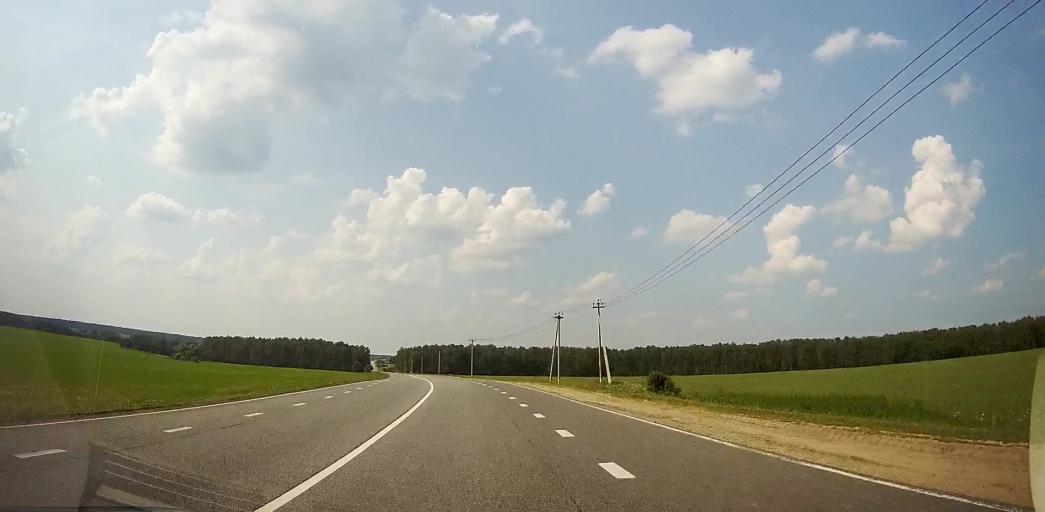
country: RU
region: Moskovskaya
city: Malino
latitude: 55.0253
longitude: 38.1742
